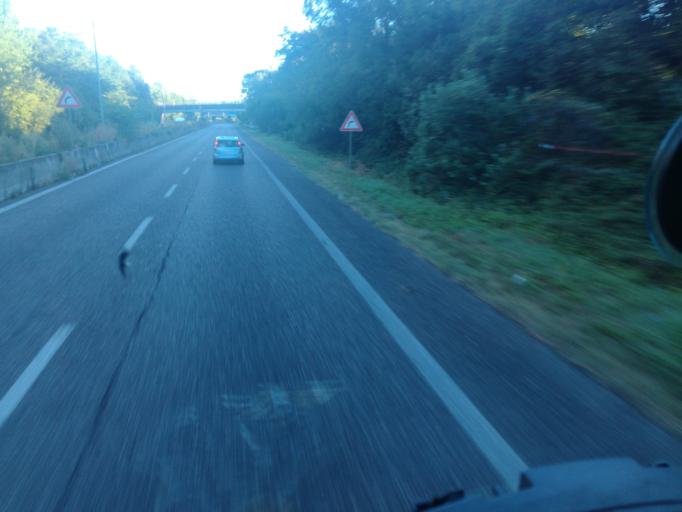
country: IT
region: Lombardy
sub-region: Provincia di Monza e Brianza
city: Seveso
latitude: 45.6472
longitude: 9.1551
